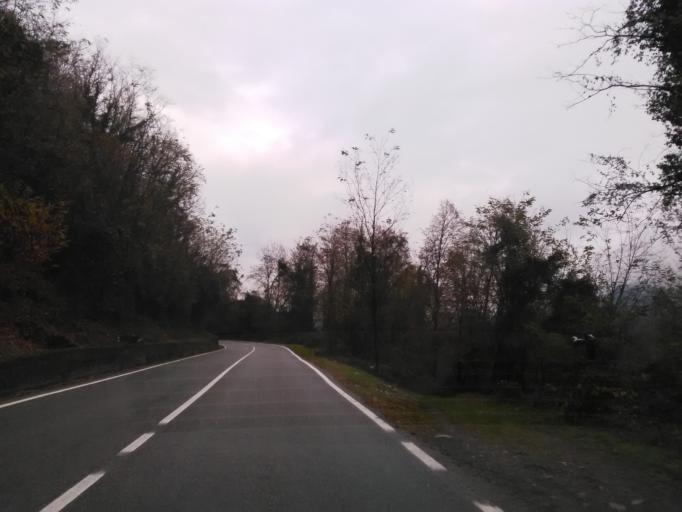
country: IT
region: Piedmont
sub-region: Provincia di Vercelli
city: Quarona
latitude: 45.7750
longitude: 8.2592
